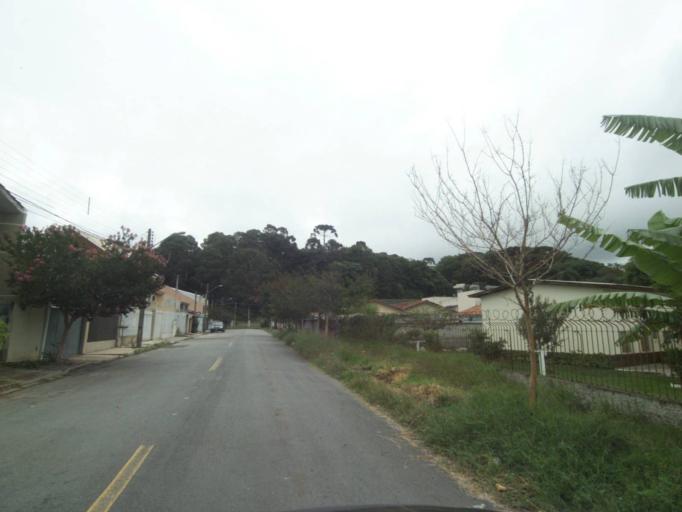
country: BR
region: Parana
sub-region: Curitiba
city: Curitiba
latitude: -25.4670
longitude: -49.3221
